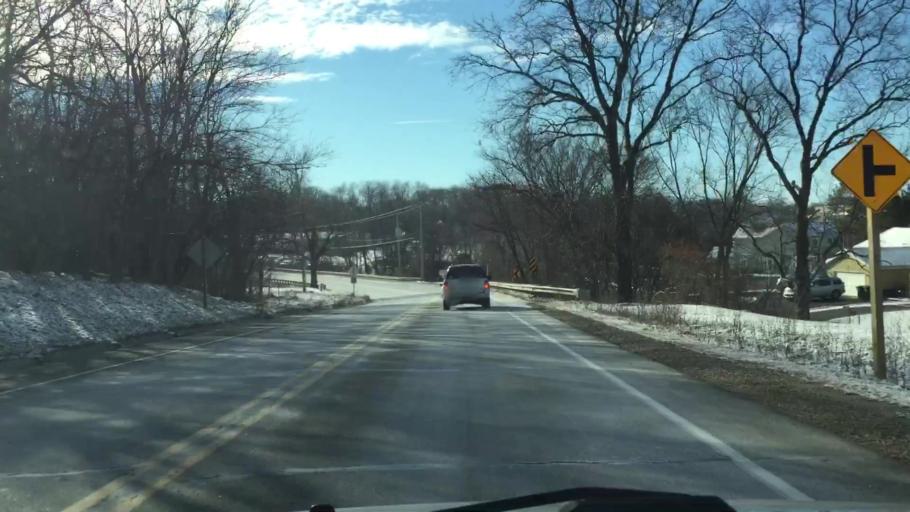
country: US
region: Wisconsin
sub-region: Walworth County
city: Elkhorn
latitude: 42.7680
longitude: -88.5556
